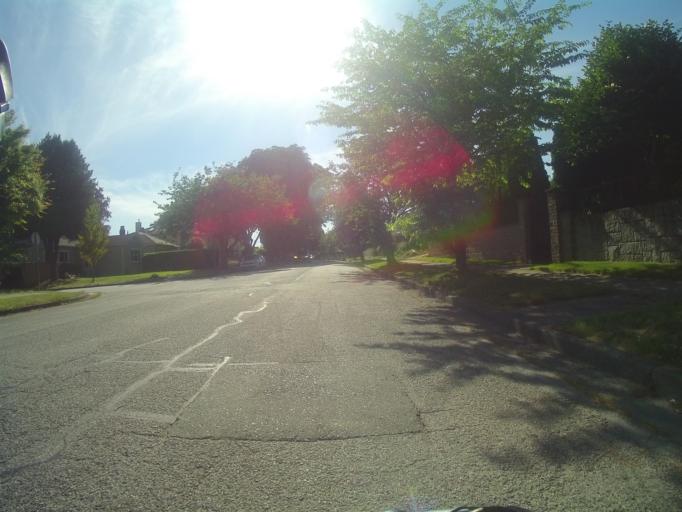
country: CA
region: British Columbia
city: Vancouver
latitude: 49.2172
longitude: -123.1310
